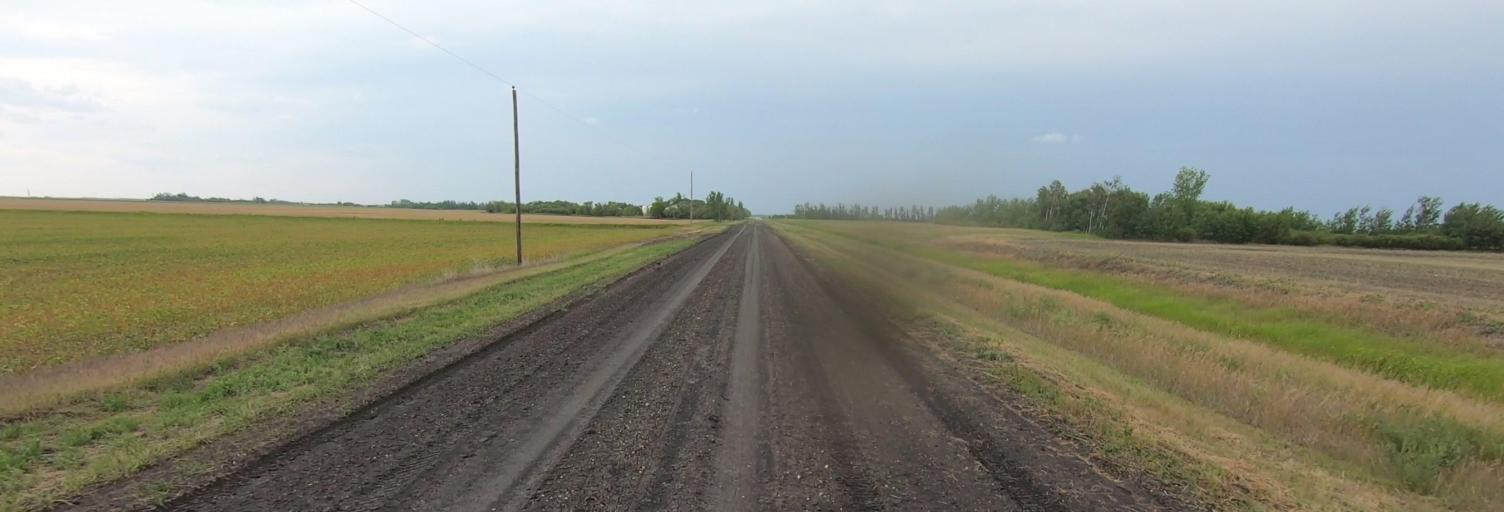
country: CA
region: Manitoba
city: Headingley
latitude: 49.7402
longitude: -97.4135
